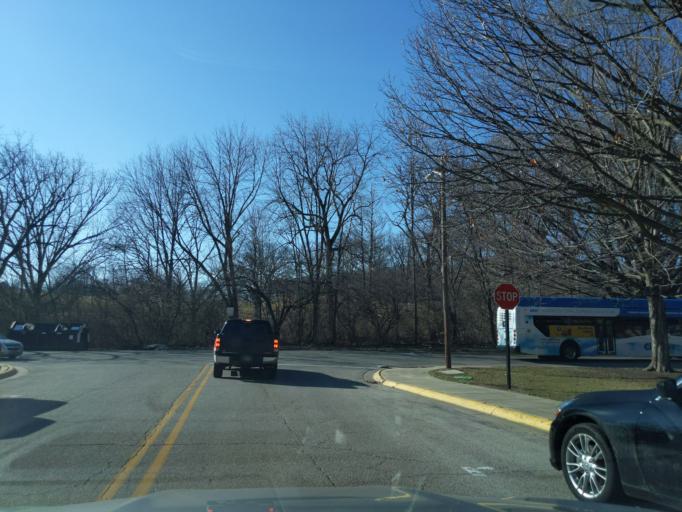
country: US
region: Indiana
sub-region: Tippecanoe County
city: West Lafayette
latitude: 40.4333
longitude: -86.9268
